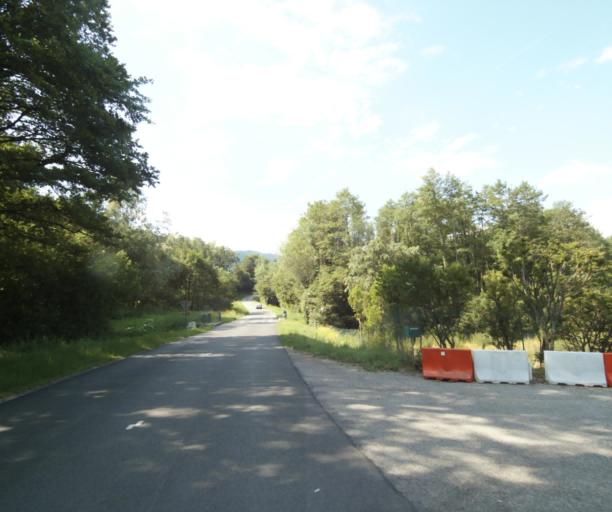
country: FR
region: Rhone-Alpes
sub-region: Departement de la Haute-Savoie
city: Allinges
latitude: 46.3338
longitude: 6.4927
